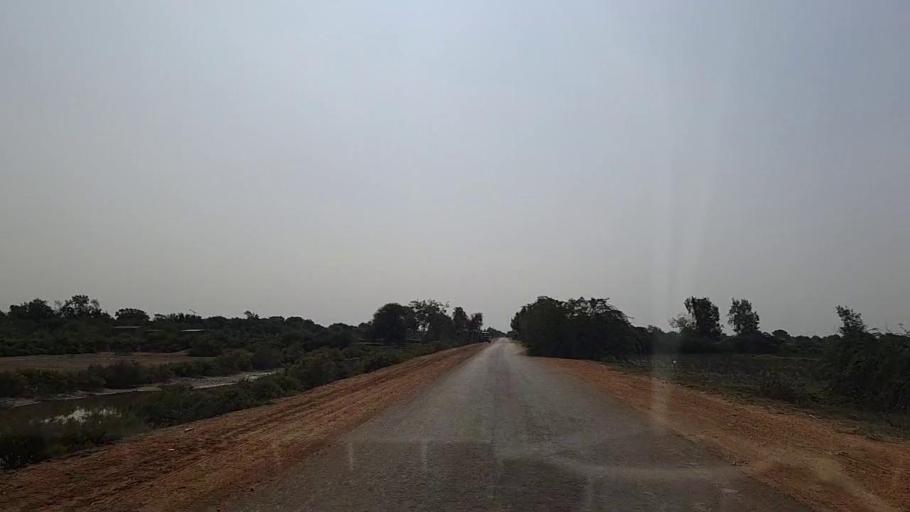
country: PK
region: Sindh
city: Chuhar Jamali
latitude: 24.2591
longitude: 67.9077
